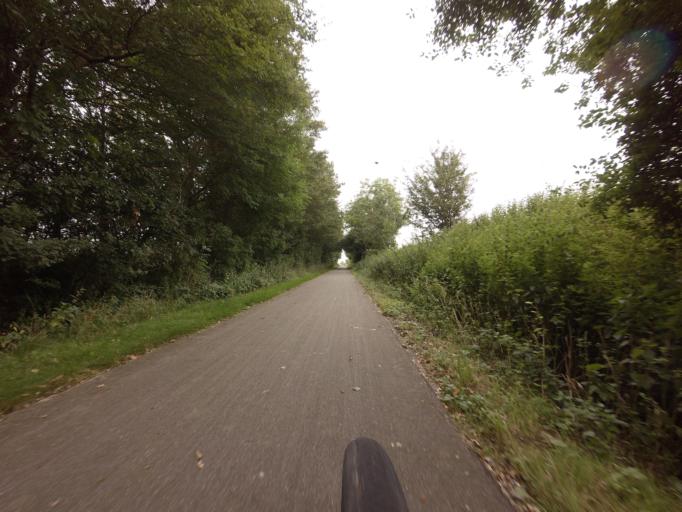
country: DK
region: Zealand
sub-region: Naestved Kommune
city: Fuglebjerg
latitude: 55.2718
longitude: 11.4660
